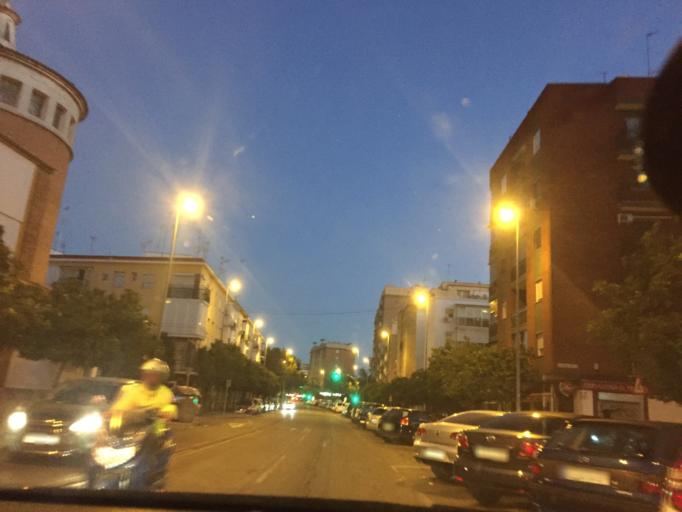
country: ES
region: Andalusia
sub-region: Provincia de Sevilla
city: Sevilla
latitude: 37.3976
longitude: -5.9758
